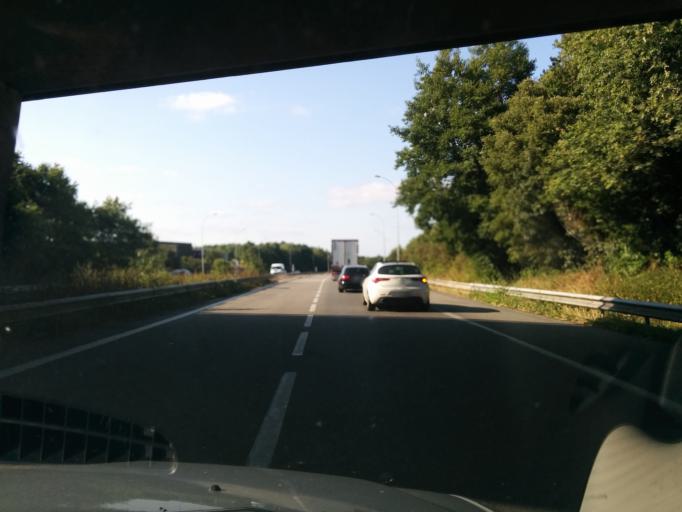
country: FR
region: Pays de la Loire
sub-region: Departement de la Loire-Atlantique
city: Carquefou
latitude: 47.2859
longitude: -1.4794
